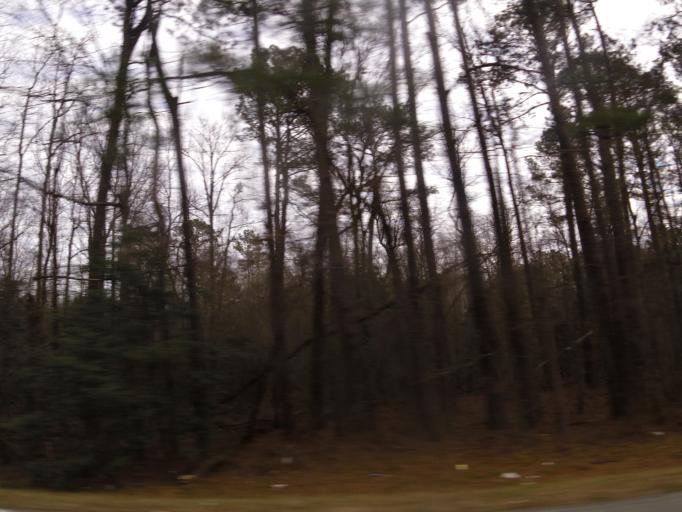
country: US
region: North Carolina
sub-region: Hertford County
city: Winton
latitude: 36.5159
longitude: -76.9853
